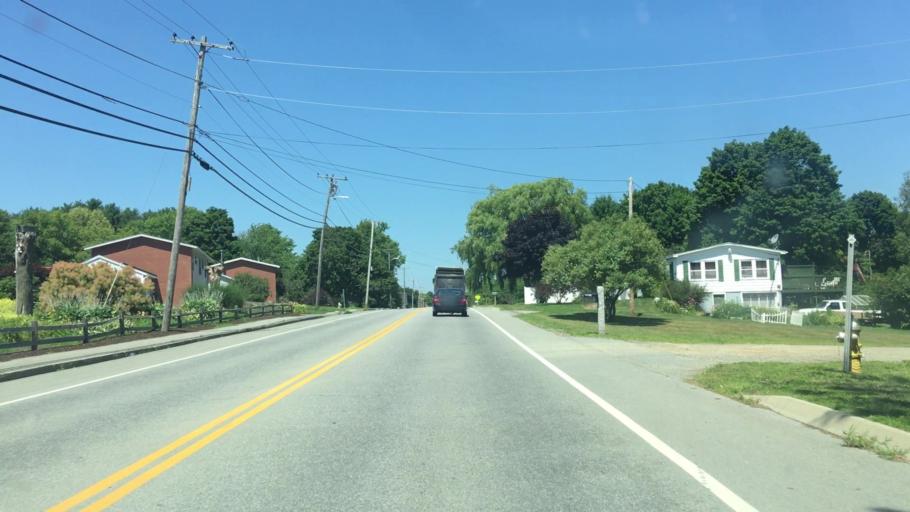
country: US
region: Maine
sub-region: Penobscot County
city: Bangor
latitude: 44.8264
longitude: -68.8114
